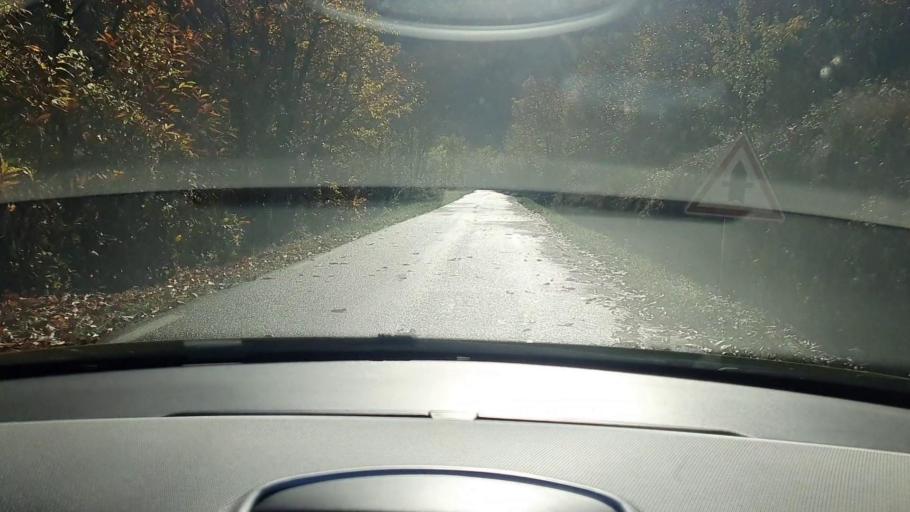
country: FR
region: Languedoc-Roussillon
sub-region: Departement du Gard
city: Valleraugue
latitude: 44.1637
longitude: 3.6374
